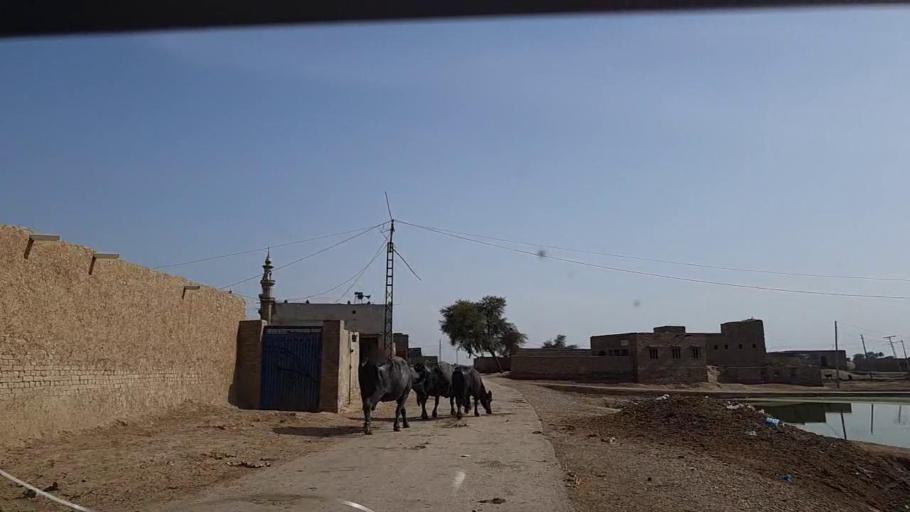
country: PK
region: Sindh
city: Phulji
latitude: 26.9911
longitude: 67.6637
